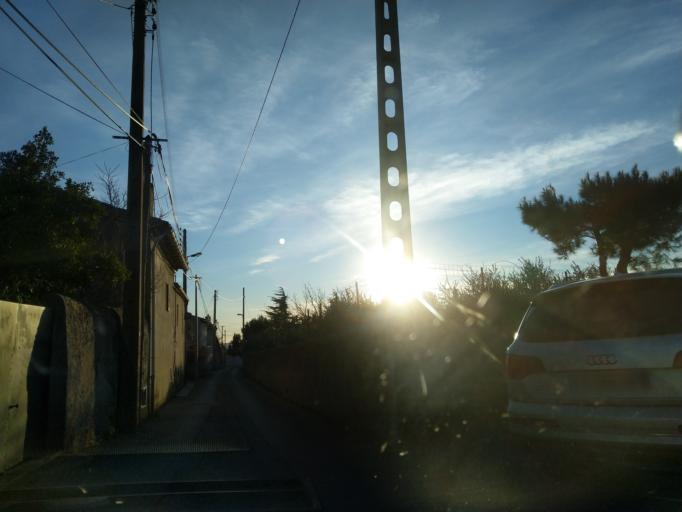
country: FR
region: Provence-Alpes-Cote d'Azur
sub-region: Departement des Bouches-du-Rhone
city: Plan-de-Cuques
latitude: 43.3526
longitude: 5.4575
